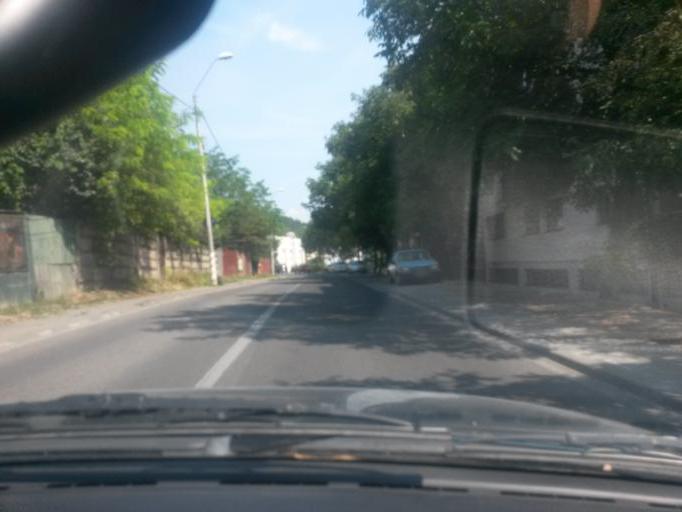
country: RO
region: Mures
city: Targu-Mures
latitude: 46.5397
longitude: 24.5765
